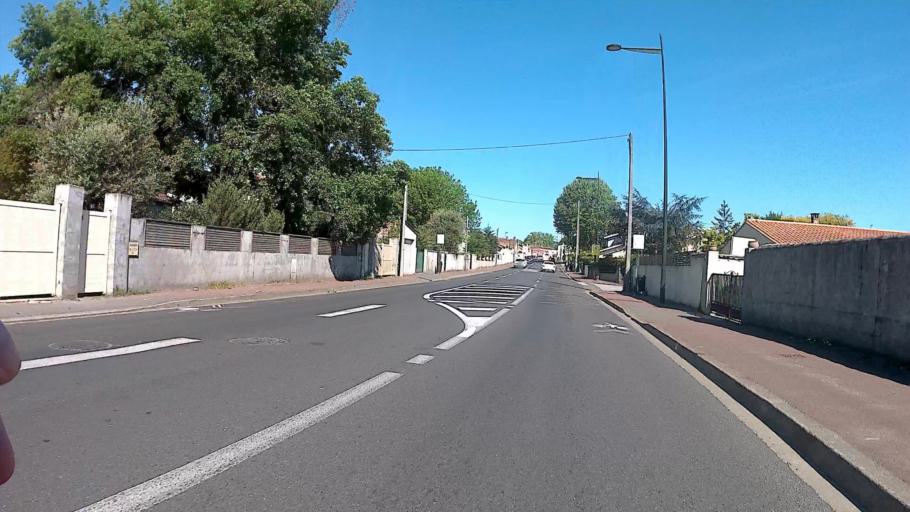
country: FR
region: Aquitaine
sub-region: Departement de la Gironde
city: Begles
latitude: 44.7981
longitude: -0.5414
